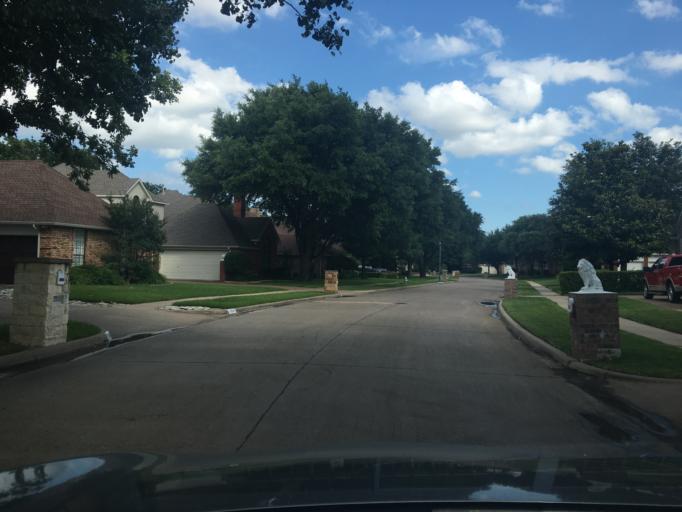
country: US
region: Texas
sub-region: Dallas County
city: Garland
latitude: 32.9363
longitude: -96.6725
